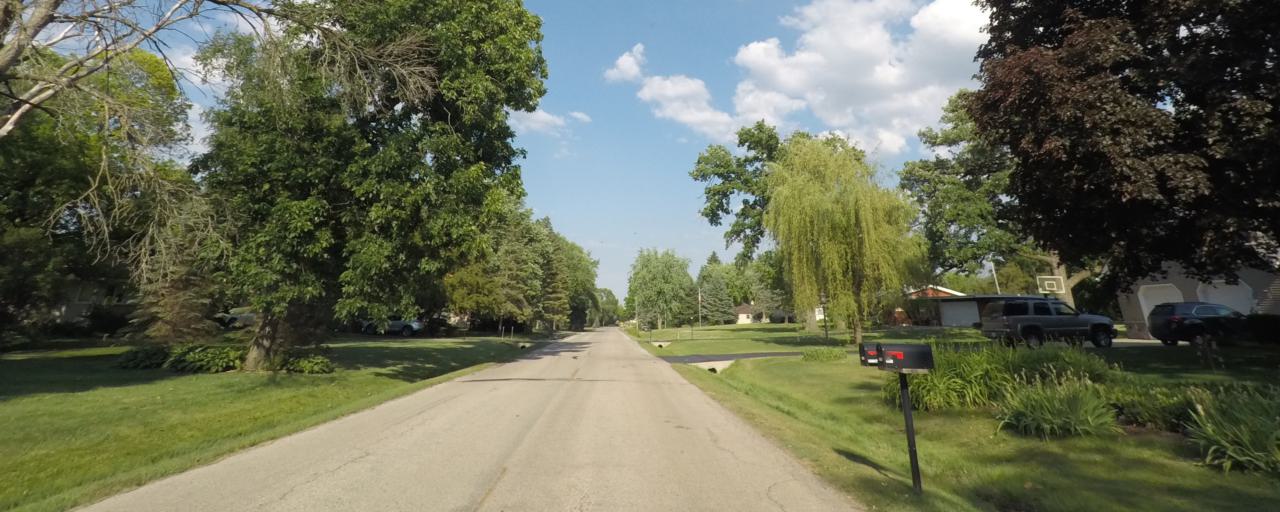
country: US
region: Wisconsin
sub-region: Waukesha County
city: Muskego
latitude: 42.9241
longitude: -88.1030
